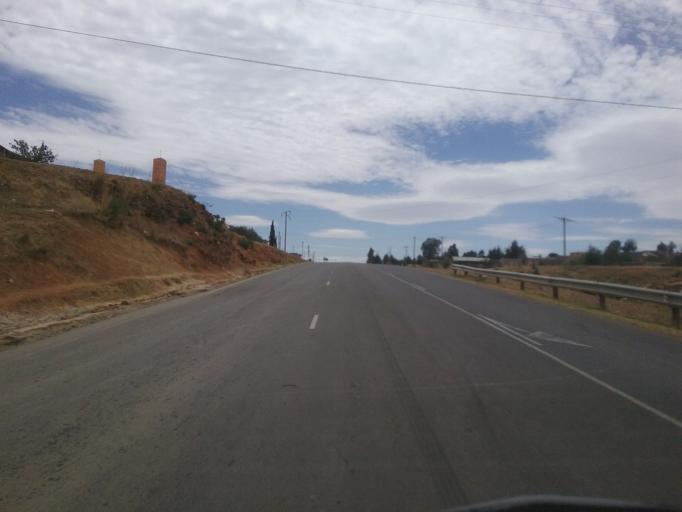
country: LS
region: Maseru
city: Maseru
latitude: -29.4936
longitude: 27.5277
